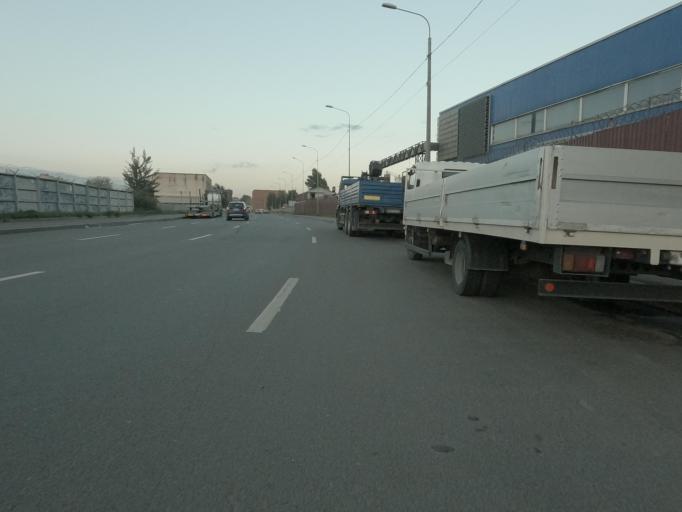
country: RU
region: St.-Petersburg
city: Vasyl'evsky Ostrov
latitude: 59.9034
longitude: 30.2382
